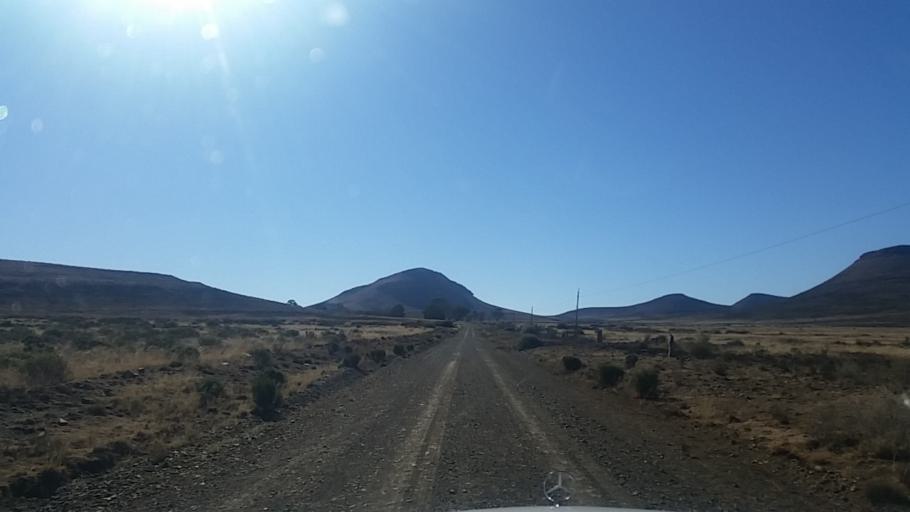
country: ZA
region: Eastern Cape
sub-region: Chris Hani District Municipality
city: Middelburg
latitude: -31.7977
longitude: 24.7204
